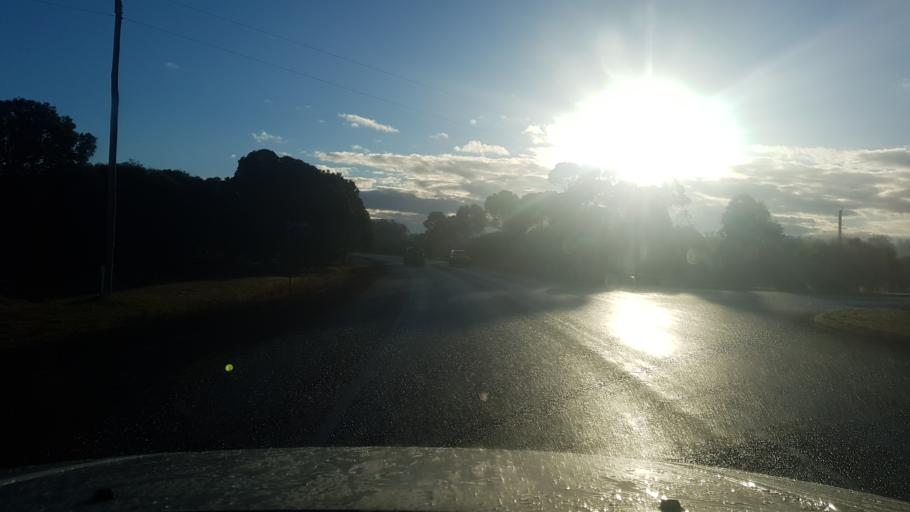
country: AU
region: Western Australia
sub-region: Busselton
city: Vasse
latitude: -33.6714
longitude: 115.2561
